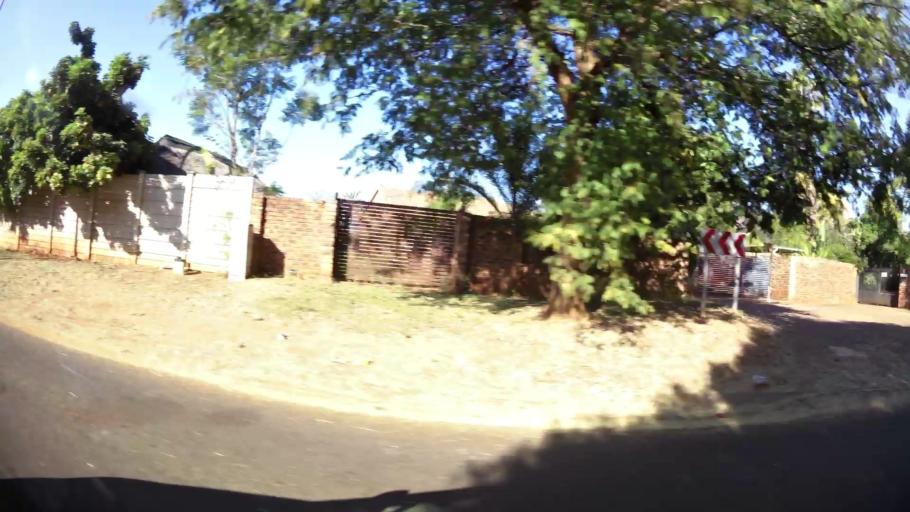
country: ZA
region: Gauteng
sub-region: City of Tshwane Metropolitan Municipality
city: Pretoria
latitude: -25.6524
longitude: 28.2390
